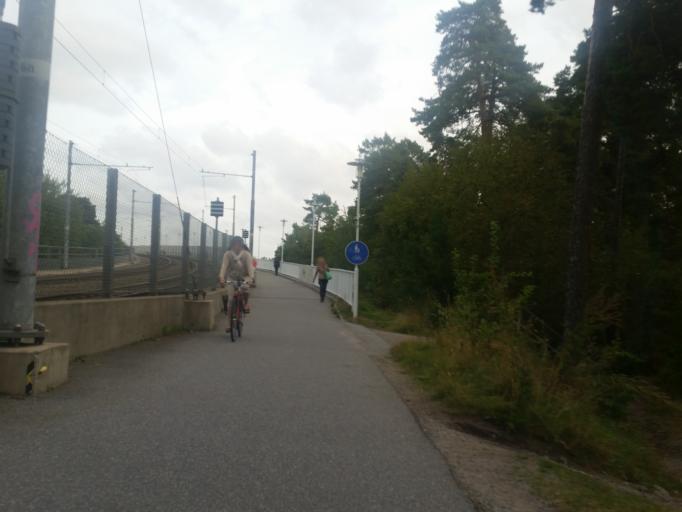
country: SE
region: Stockholm
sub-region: Sundbybergs Kommun
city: Sundbyberg
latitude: 59.3279
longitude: 17.9828
